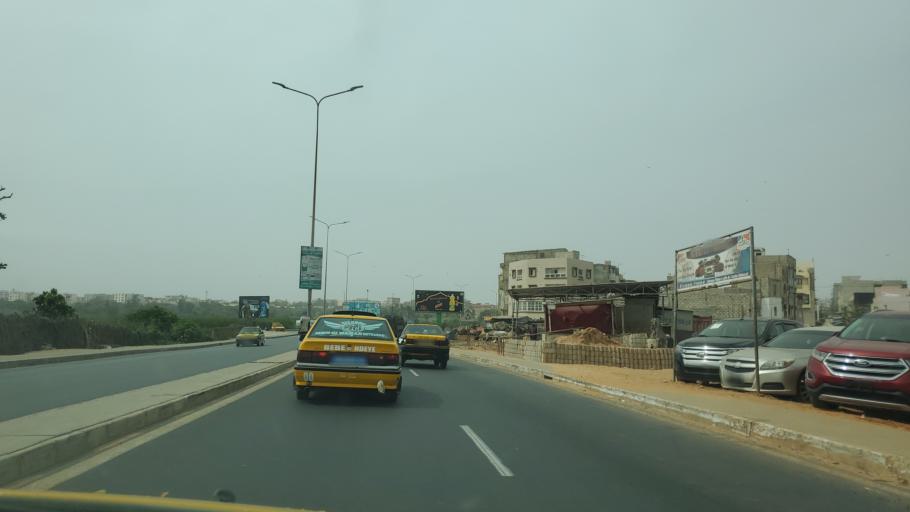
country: SN
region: Dakar
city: Pikine
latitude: 14.7634
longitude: -17.3999
